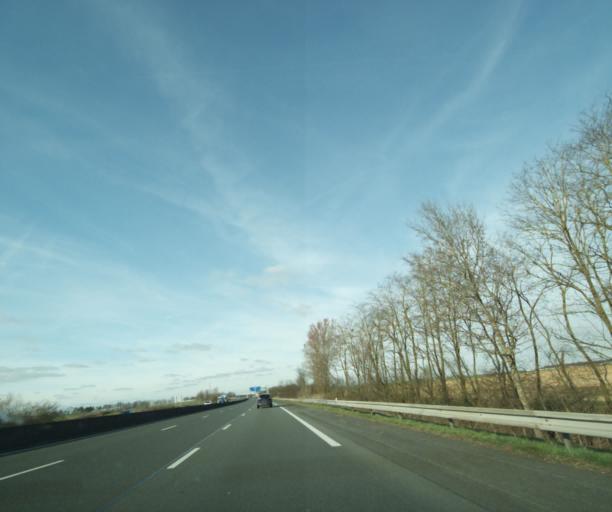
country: FR
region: Ile-de-France
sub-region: Departement de l'Essonne
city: Corbreuse
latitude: 48.4488
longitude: 1.9106
